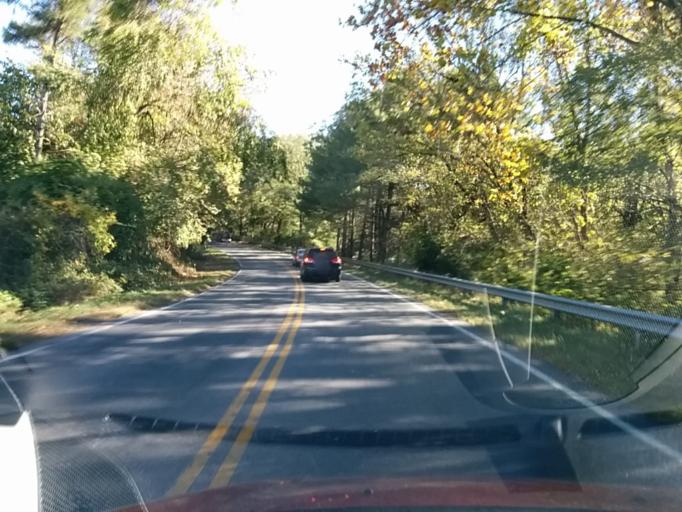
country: US
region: Virginia
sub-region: Roanoke County
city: Hollins
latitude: 37.3521
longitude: -79.9284
